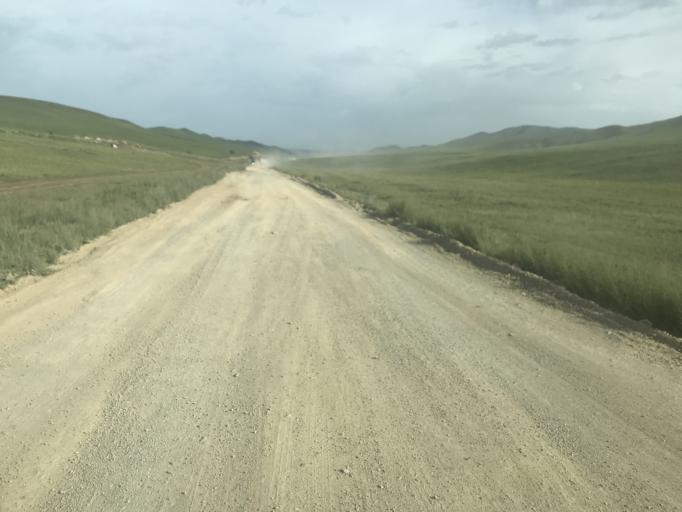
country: MN
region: Central Aimak
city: Javhlant
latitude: 48.7415
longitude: 106.1280
